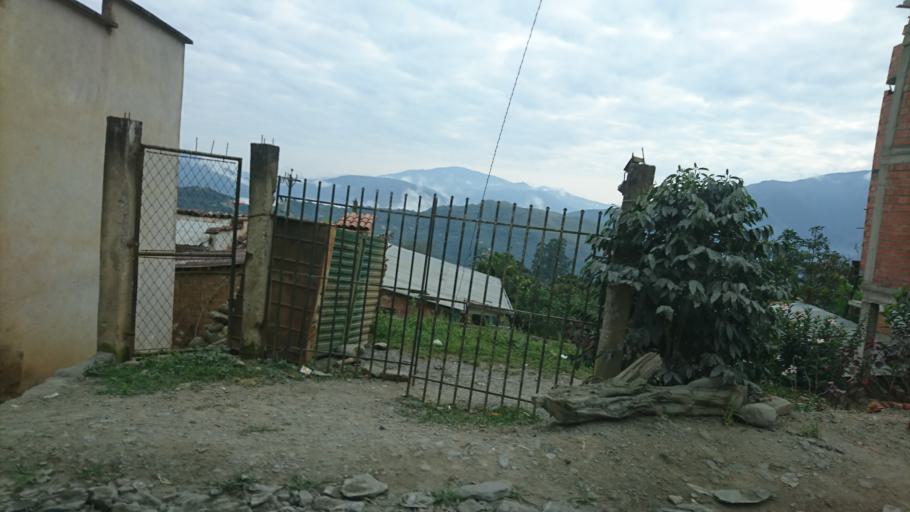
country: BO
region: La Paz
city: Coroico
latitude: -16.2001
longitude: -67.6984
